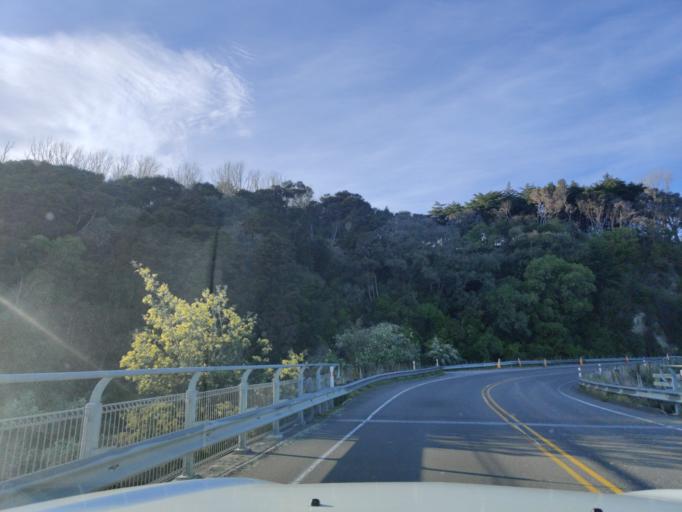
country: NZ
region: Manawatu-Wanganui
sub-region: Palmerston North City
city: Palmerston North
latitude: -40.2817
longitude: 175.7715
